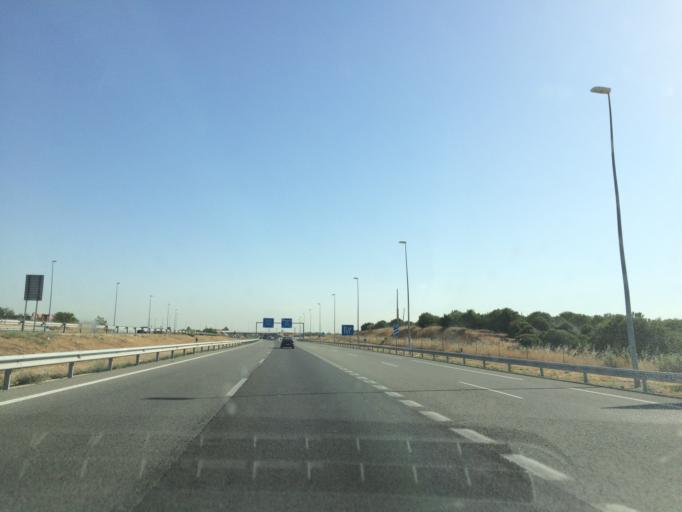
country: ES
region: Madrid
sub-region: Provincia de Madrid
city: Navalcarnero
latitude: 40.2609
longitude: -4.0437
